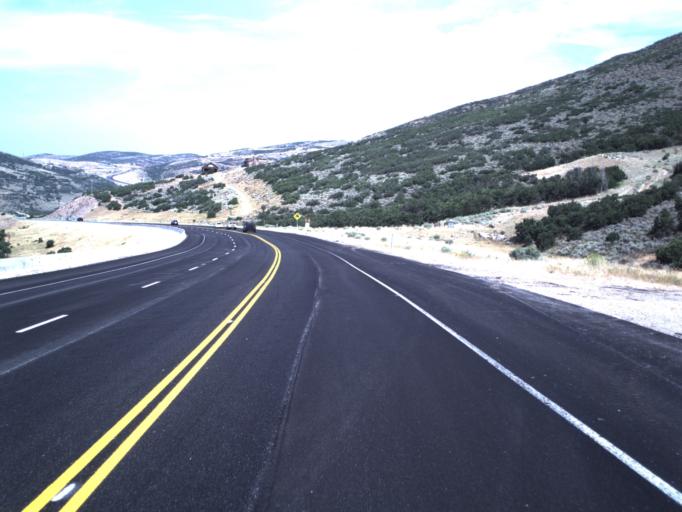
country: US
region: Utah
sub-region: Summit County
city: Park City
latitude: 40.6471
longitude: -111.4008
